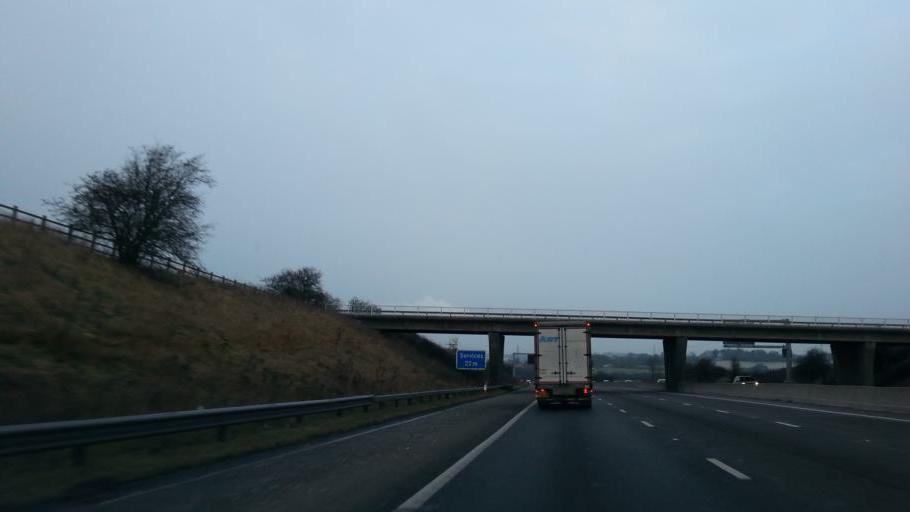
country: GB
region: England
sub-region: Rotherham
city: Ulley
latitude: 53.3874
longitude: -1.2797
